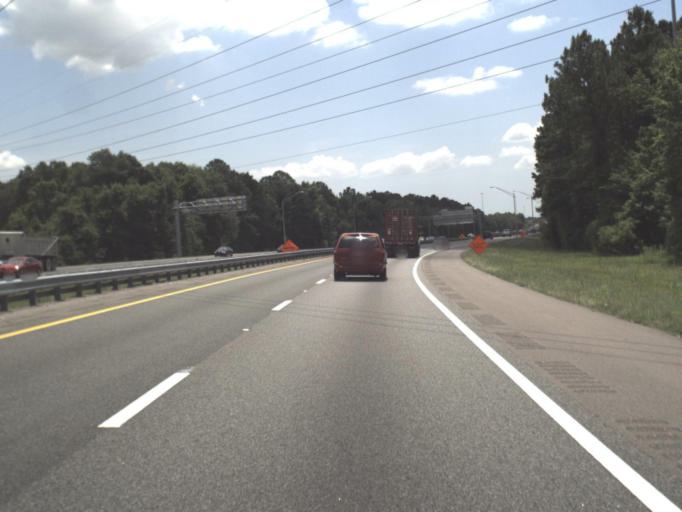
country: US
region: Florida
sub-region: Duval County
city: Jacksonville
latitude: 30.4550
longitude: -81.6242
